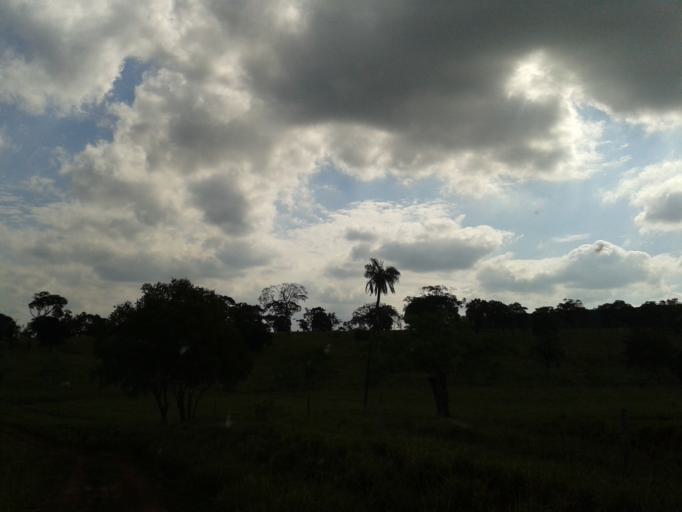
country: BR
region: Minas Gerais
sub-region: Campina Verde
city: Campina Verde
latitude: -19.3930
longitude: -49.6851
